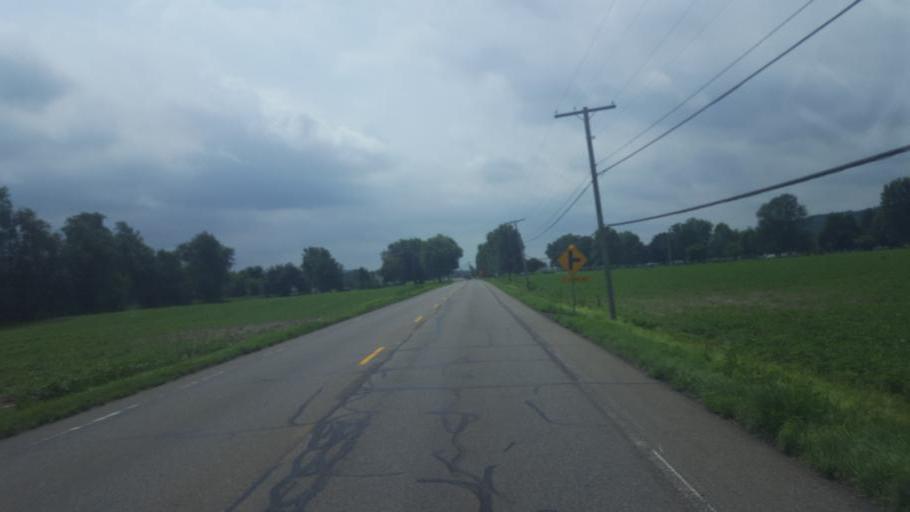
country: US
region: Ohio
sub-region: Licking County
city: Utica
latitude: 40.1579
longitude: -82.4252
